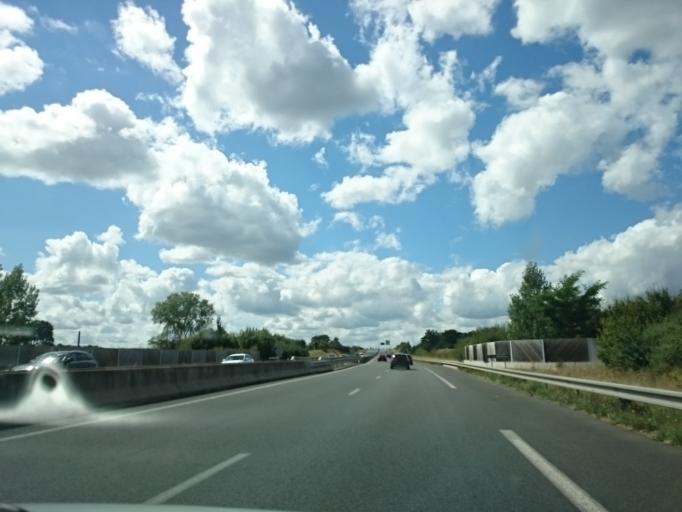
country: FR
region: Pays de la Loire
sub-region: Departement de Maine-et-Loire
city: Avrille
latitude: 47.4949
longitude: -0.6087
